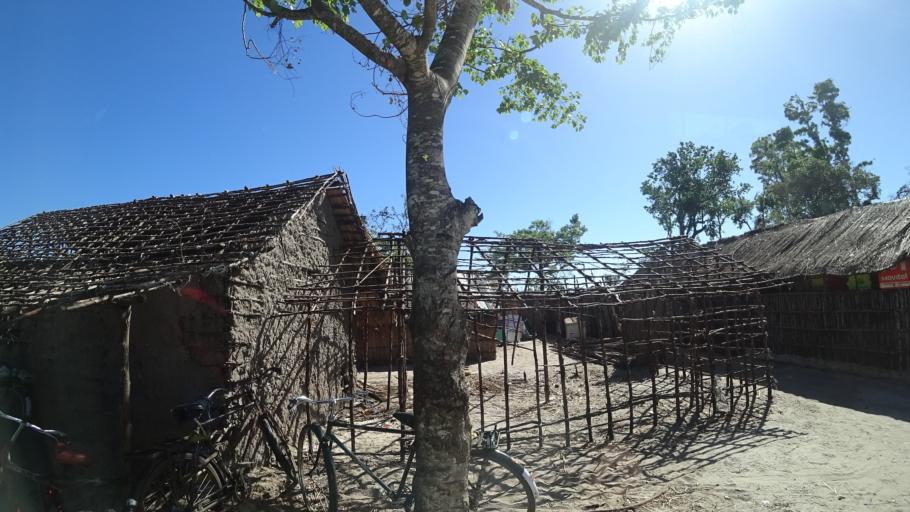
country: MZ
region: Sofala
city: Beira
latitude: -19.5767
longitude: 35.2628
